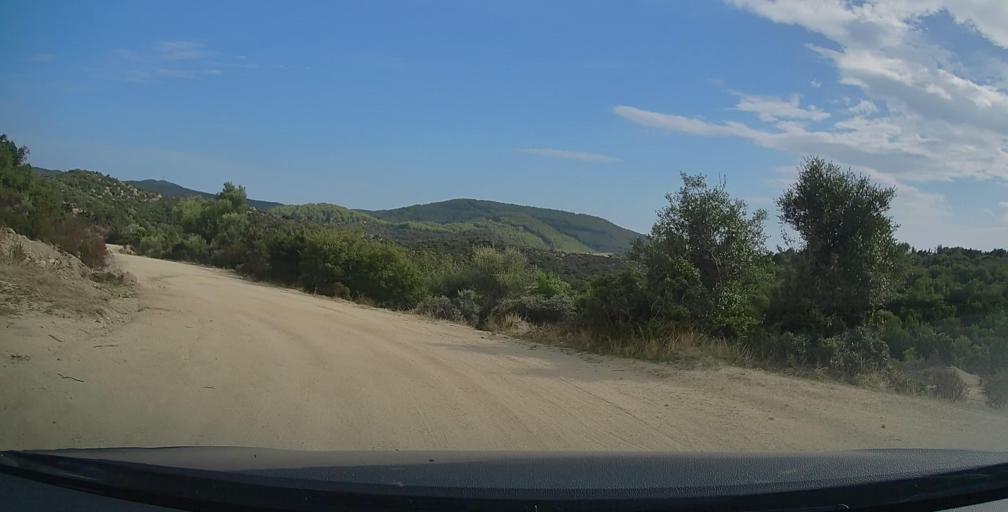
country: GR
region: Central Macedonia
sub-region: Nomos Chalkidikis
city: Sykia
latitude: 40.0025
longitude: 23.9243
